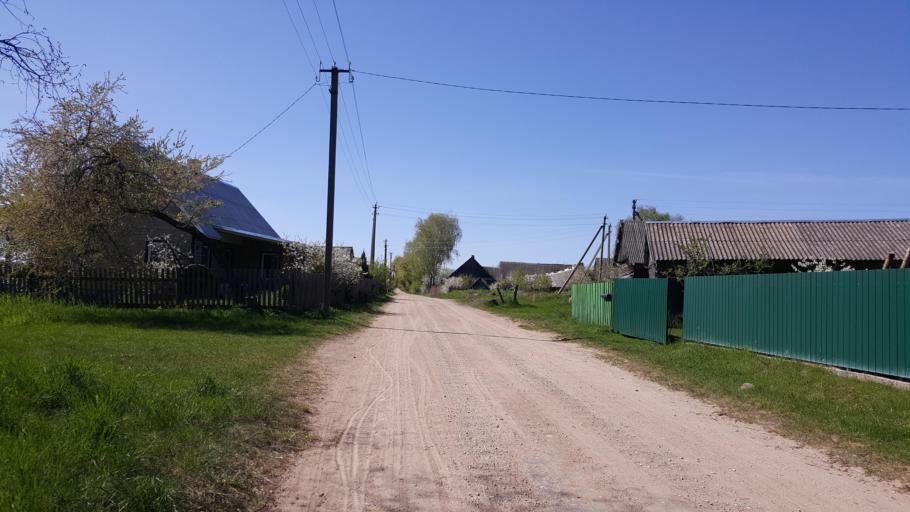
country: BY
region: Brest
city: Kamyanyets
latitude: 52.4529
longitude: 23.8862
